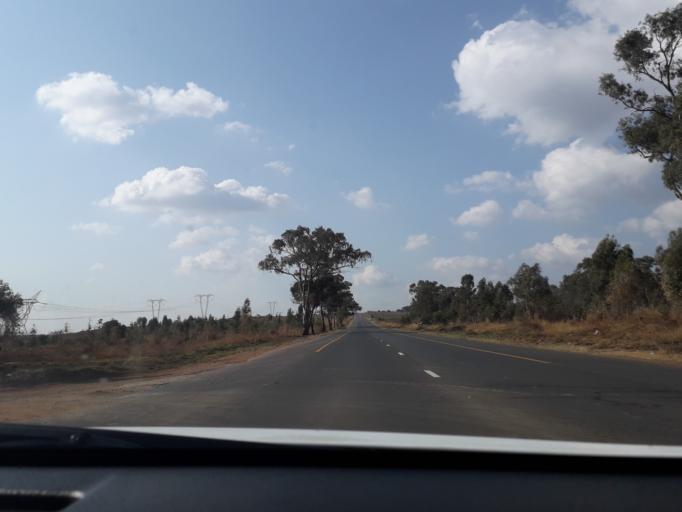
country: ZA
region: Gauteng
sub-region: Ekurhuleni Metropolitan Municipality
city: Tembisa
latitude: -25.9163
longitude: 28.2461
